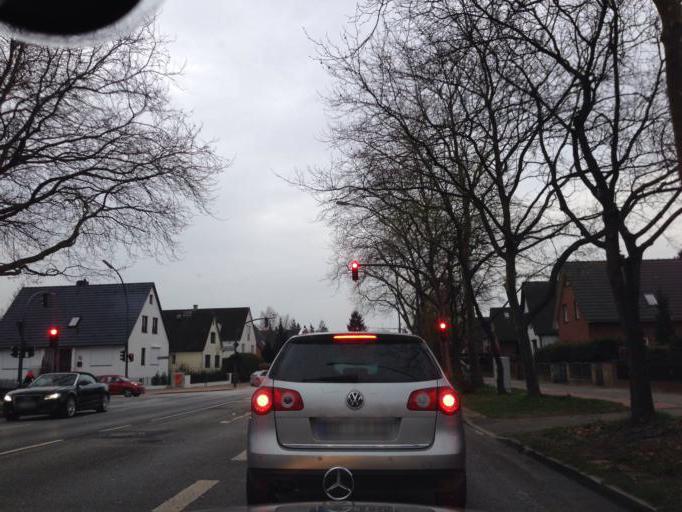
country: DE
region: Hamburg
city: Farmsen-Berne
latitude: 53.6206
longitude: 10.1489
